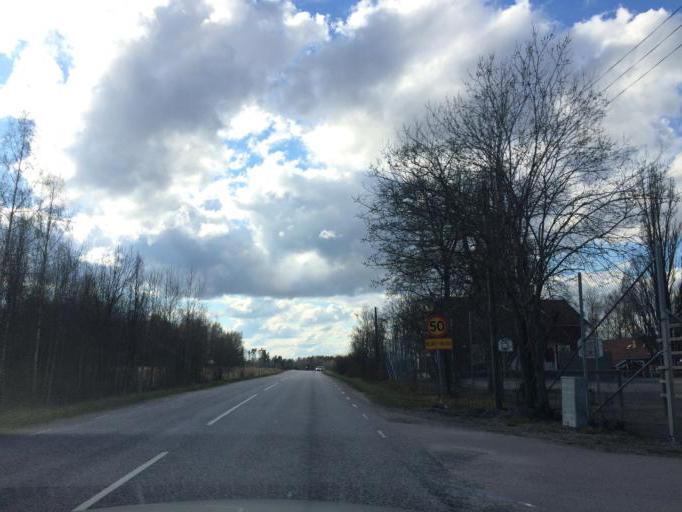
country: SE
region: Soedermanland
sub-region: Eskilstuna Kommun
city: Eskilstuna
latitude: 59.4157
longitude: 16.5577
